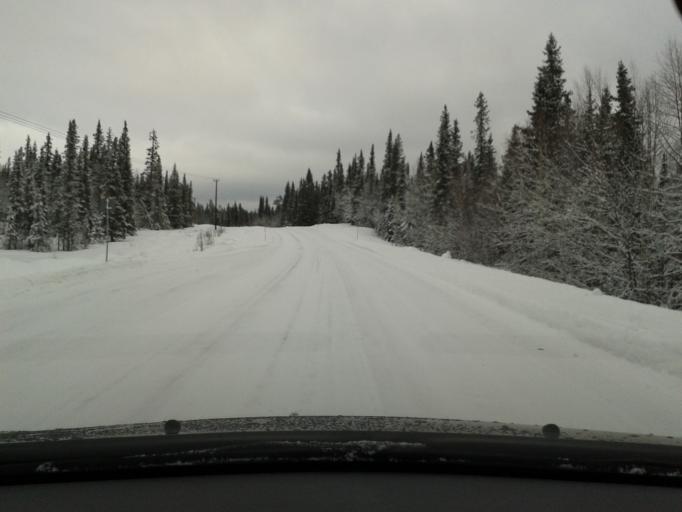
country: SE
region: Vaesterbotten
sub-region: Vilhelmina Kommun
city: Sjoberg
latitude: 65.2391
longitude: 15.7859
